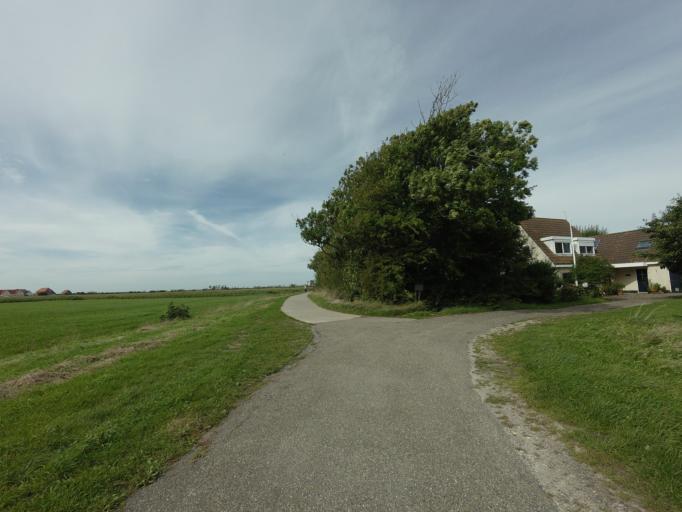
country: NL
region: North Holland
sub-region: Gemeente Texel
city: Den Burg
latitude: 53.0723
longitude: 4.8107
